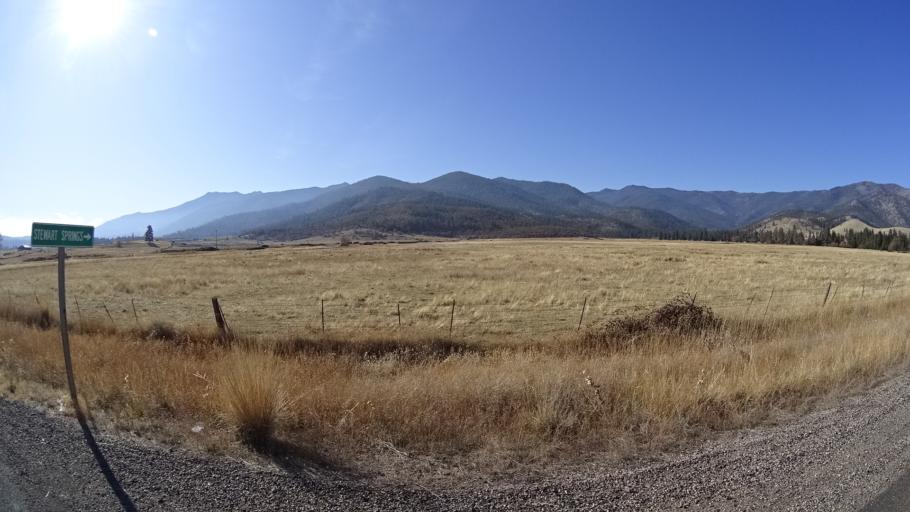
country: US
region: California
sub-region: Siskiyou County
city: Weed
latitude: 41.4451
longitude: -122.4438
